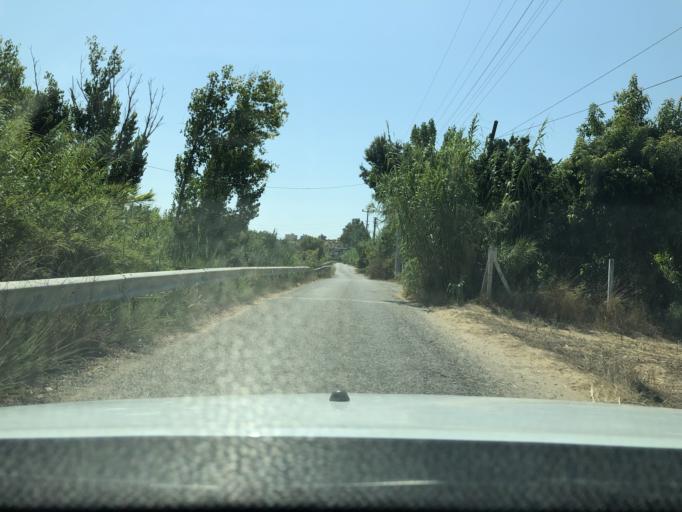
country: TR
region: Antalya
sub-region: Manavgat
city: Manavgat
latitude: 36.8059
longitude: 31.4659
